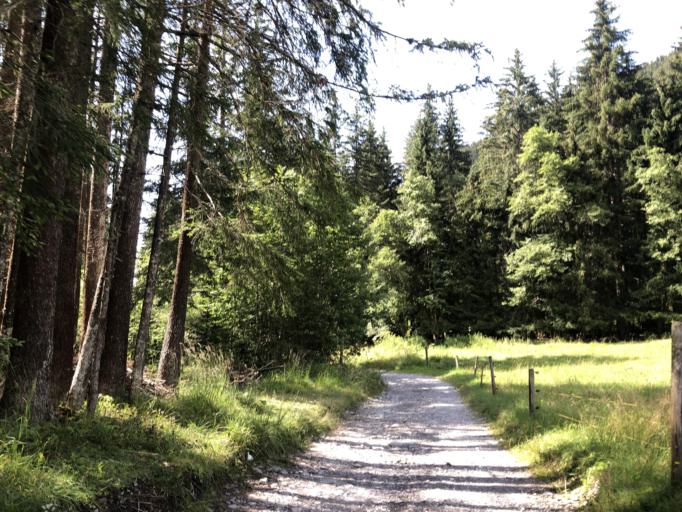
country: FR
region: Rhone-Alpes
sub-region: Departement de la Haute-Savoie
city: Megeve
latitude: 45.8307
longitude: 6.6613
